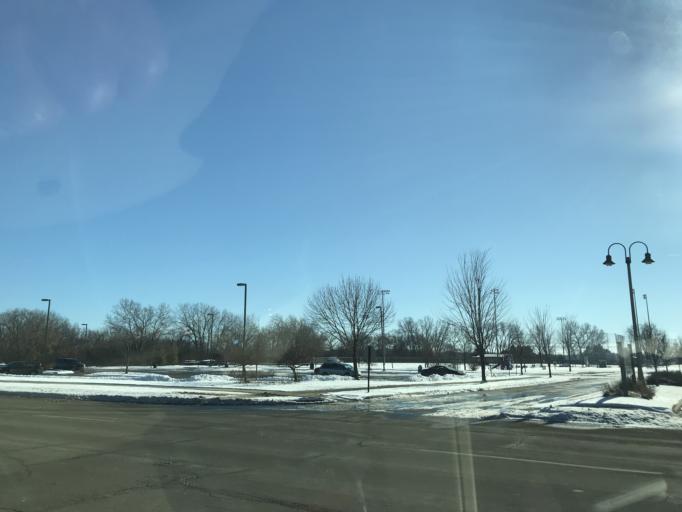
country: US
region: Wisconsin
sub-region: Dane County
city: Monona
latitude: 43.0481
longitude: -89.3191
